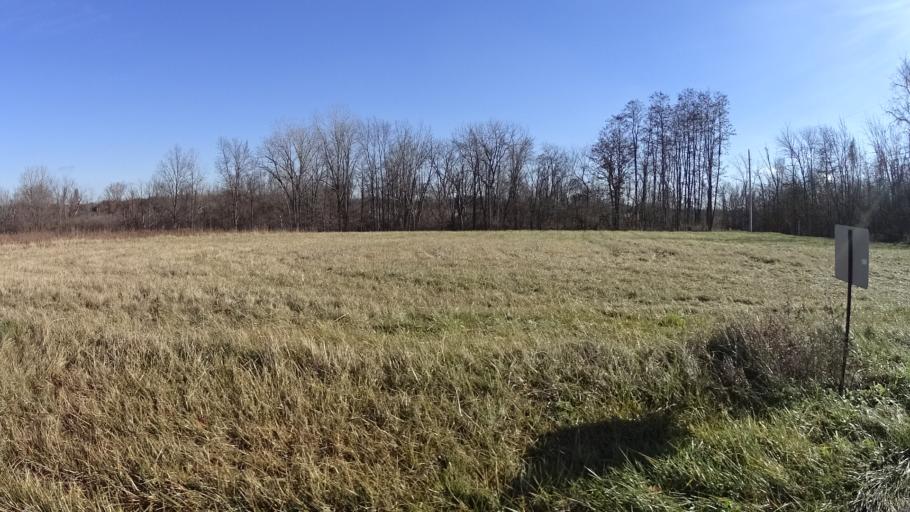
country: US
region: Ohio
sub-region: Lorain County
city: Wellington
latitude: 41.0736
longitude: -82.2795
